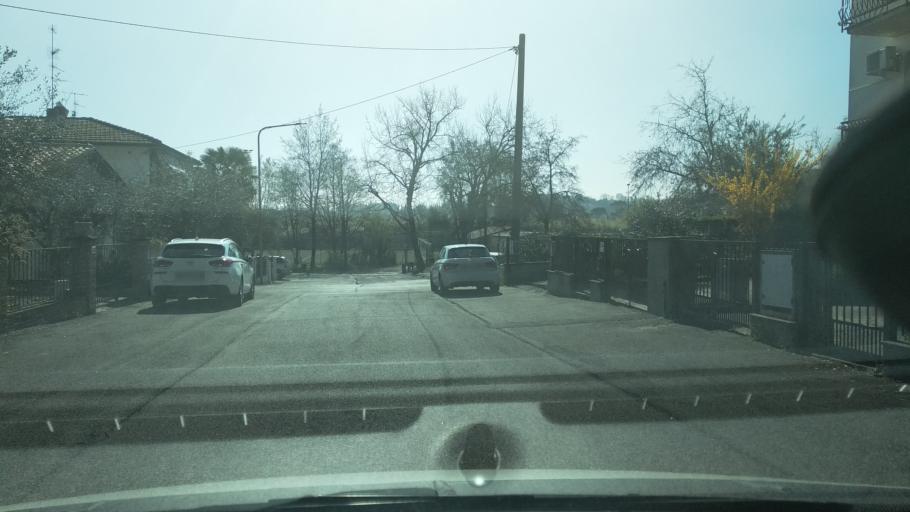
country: IT
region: Emilia-Romagna
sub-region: Provincia di Ravenna
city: Faenza
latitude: 44.2575
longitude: 11.8693
